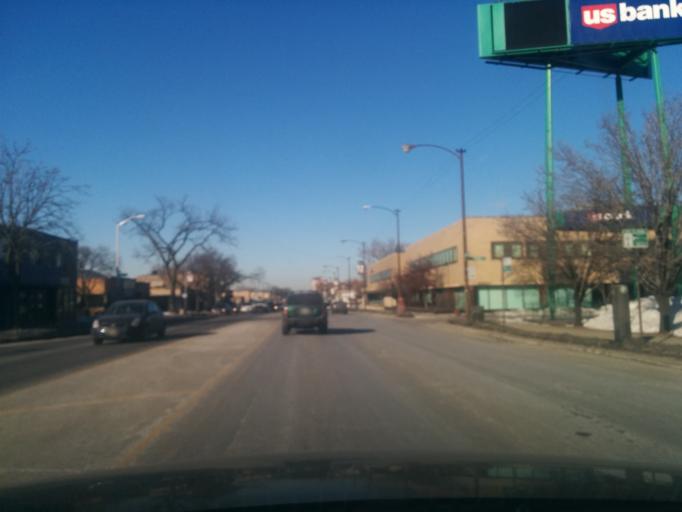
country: US
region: Illinois
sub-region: Cook County
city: Elmwood Park
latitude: 41.9091
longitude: -87.7918
